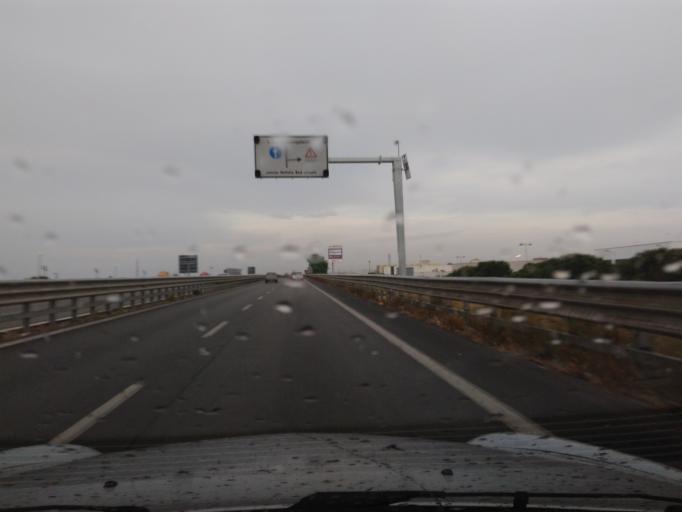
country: IT
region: Apulia
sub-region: Provincia di Bari
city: Molfetta
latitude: 41.2061
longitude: 16.5631
